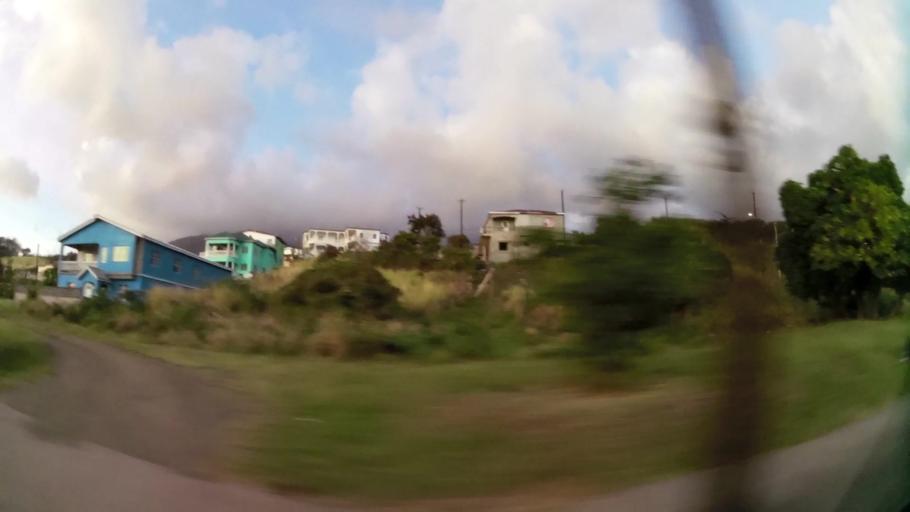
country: KN
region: Saint Thomas Middle Island
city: Middle Island
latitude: 17.3257
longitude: -62.8111
